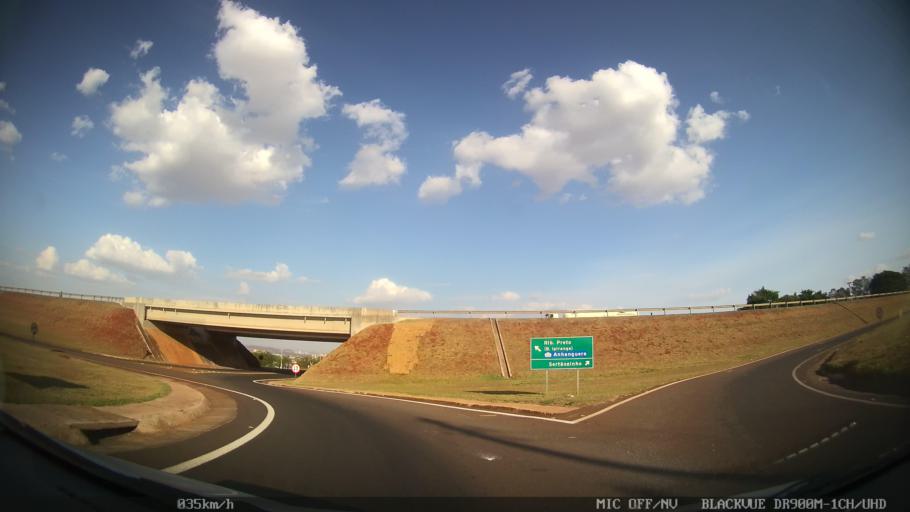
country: BR
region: Sao Paulo
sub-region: Ribeirao Preto
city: Ribeirao Preto
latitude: -21.1263
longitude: -47.8447
